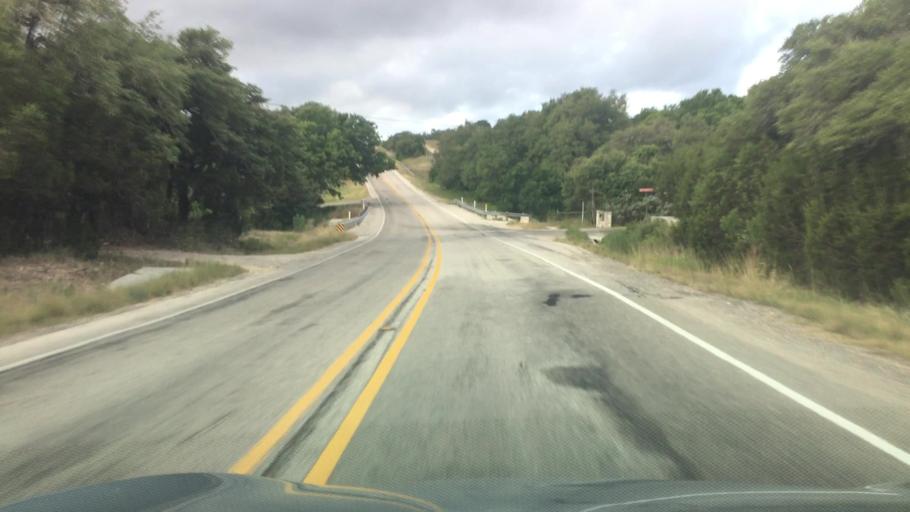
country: US
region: Texas
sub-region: Hays County
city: Dripping Springs
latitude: 30.1543
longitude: -98.2527
